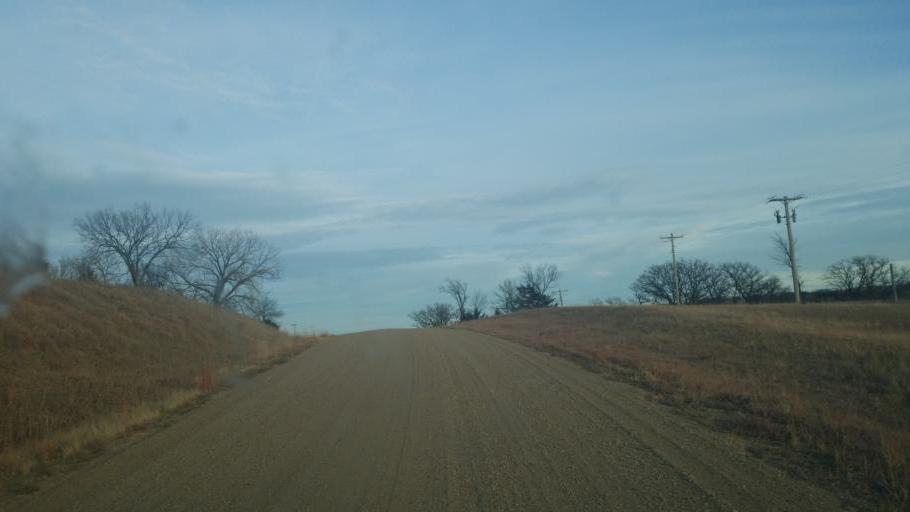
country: US
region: Nebraska
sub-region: Knox County
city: Center
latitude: 42.6918
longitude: -97.8003
